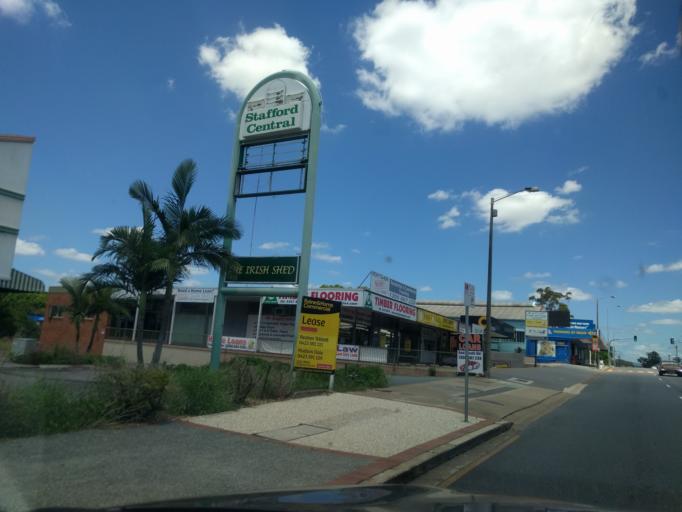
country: AU
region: Queensland
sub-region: Brisbane
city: Stafford
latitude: -27.4110
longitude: 153.0203
